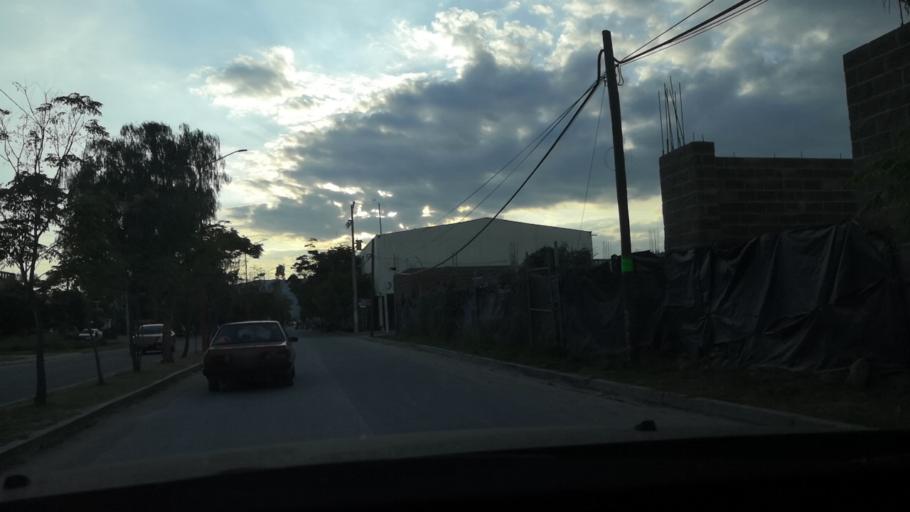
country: MX
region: Guanajuato
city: San Francisco del Rincon
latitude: 21.0204
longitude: -101.8460
